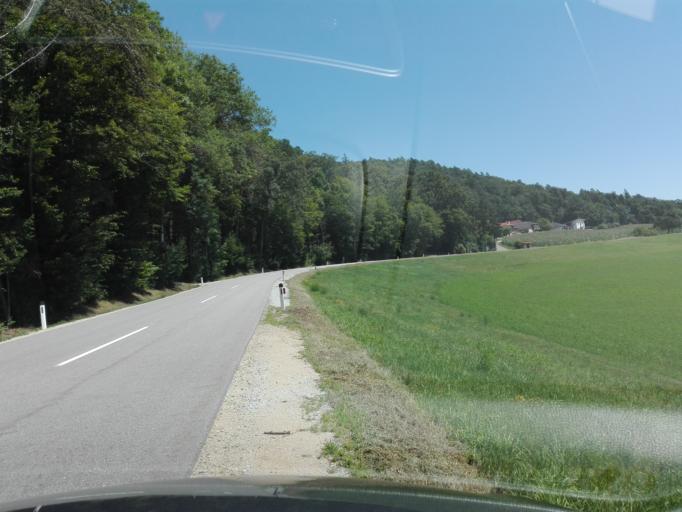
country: AT
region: Upper Austria
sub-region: Politischer Bezirk Urfahr-Umgebung
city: Gallneukirchen
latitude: 48.3329
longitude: 14.3996
